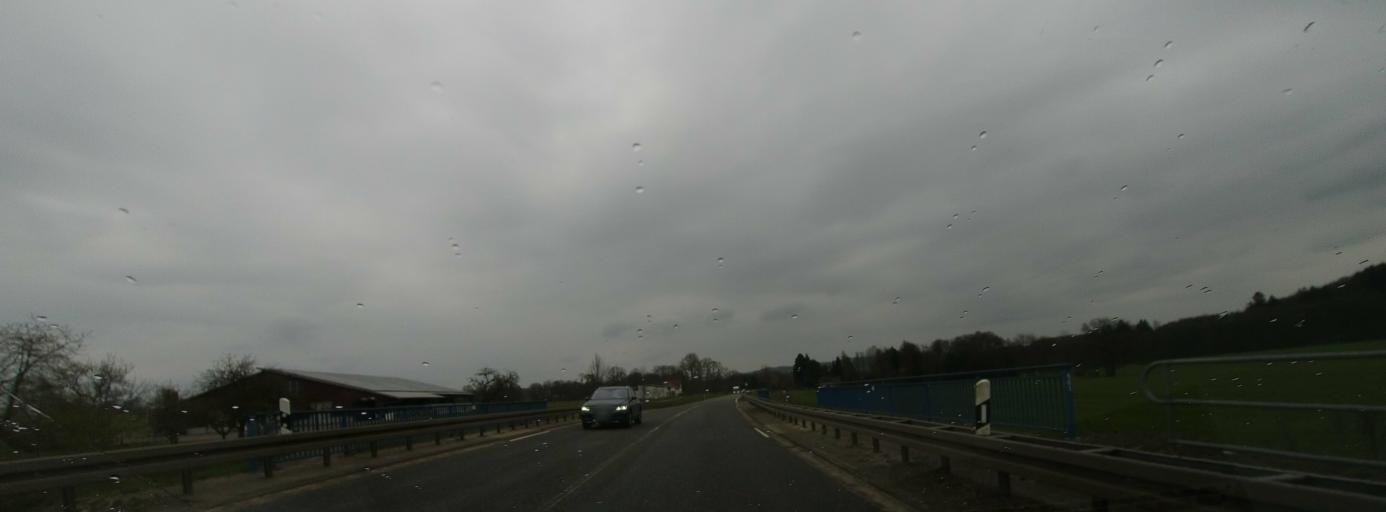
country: DE
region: Saarland
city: Weiskirchen
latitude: 49.4973
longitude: 6.8109
